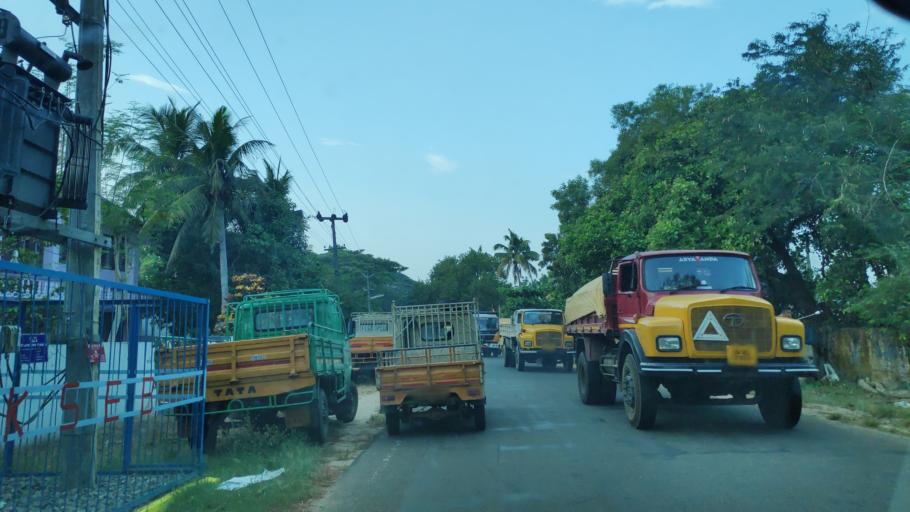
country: IN
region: Kerala
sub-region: Alappuzha
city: Shertallai
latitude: 9.6398
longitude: 76.3714
